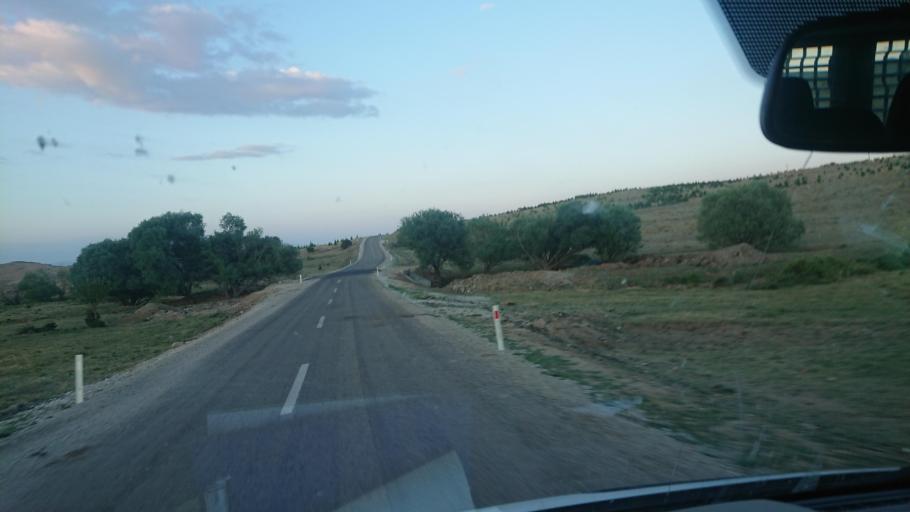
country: TR
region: Aksaray
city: Sariyahsi
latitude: 38.9685
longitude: 33.7984
